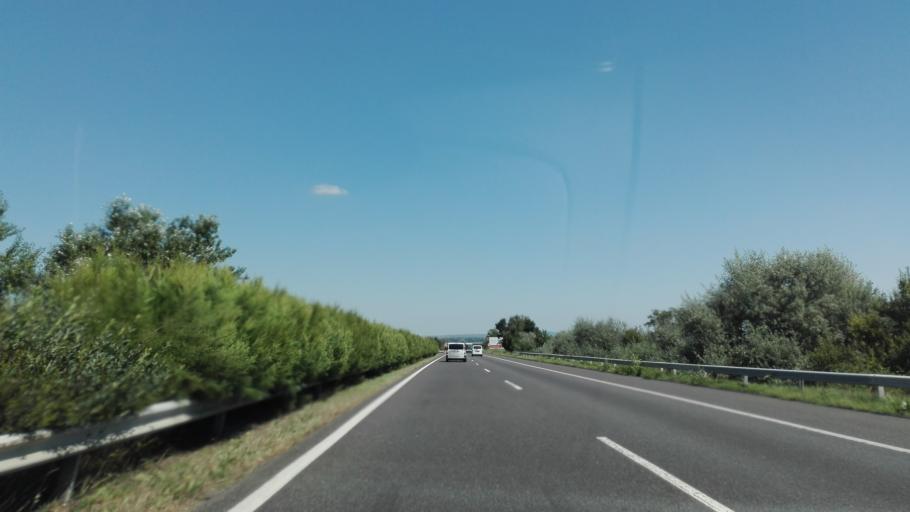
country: HU
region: Fejer
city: Szabadbattyan
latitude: 47.0835
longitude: 18.3573
